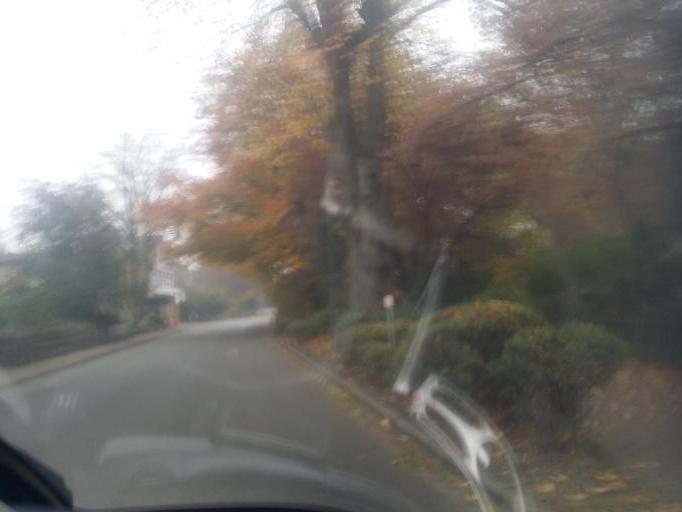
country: DE
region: Schleswig-Holstein
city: Satrup
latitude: 54.6929
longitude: 9.5990
